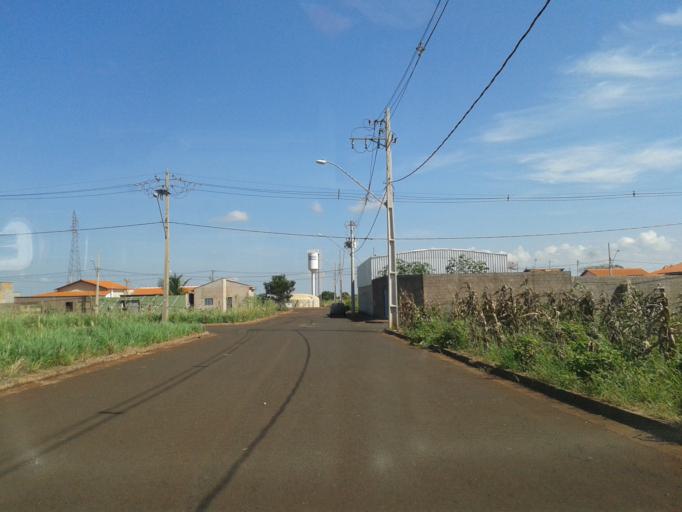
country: BR
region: Minas Gerais
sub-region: Centralina
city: Centralina
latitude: -18.5990
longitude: -49.1938
